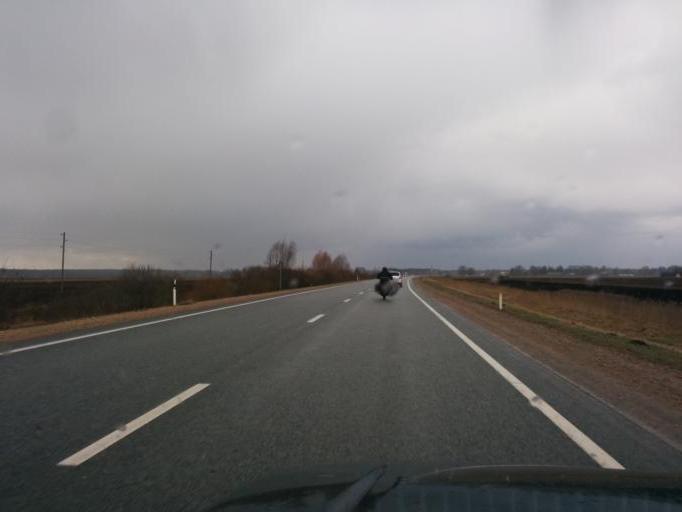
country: LV
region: Marupe
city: Marupe
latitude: 56.8630
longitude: 23.9804
